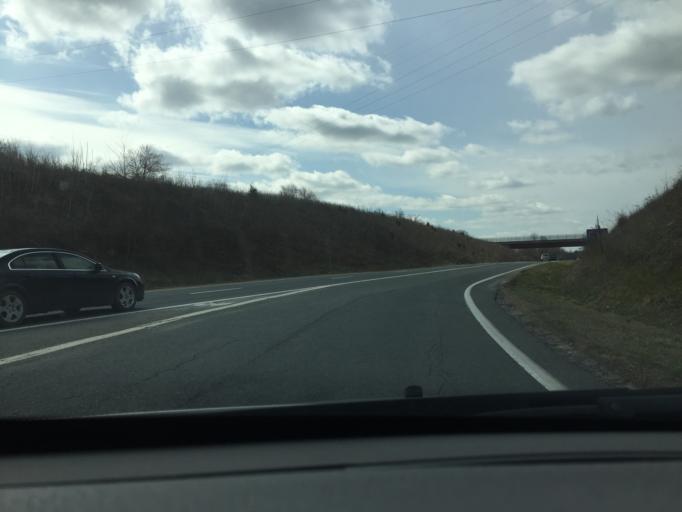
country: US
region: Virginia
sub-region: City of Lynchburg
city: West Lynchburg
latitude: 37.3544
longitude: -79.1726
